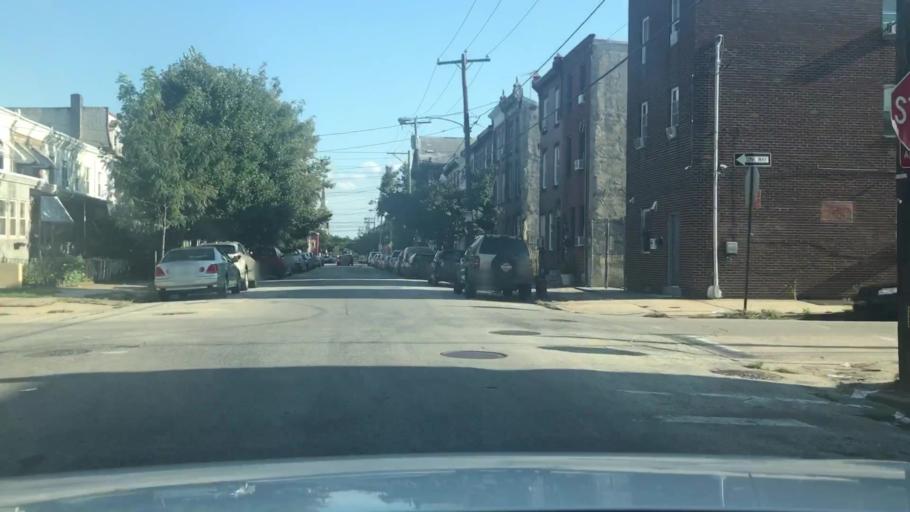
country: US
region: Pennsylvania
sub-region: Philadelphia County
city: Philadelphia
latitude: 39.9857
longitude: -75.1280
